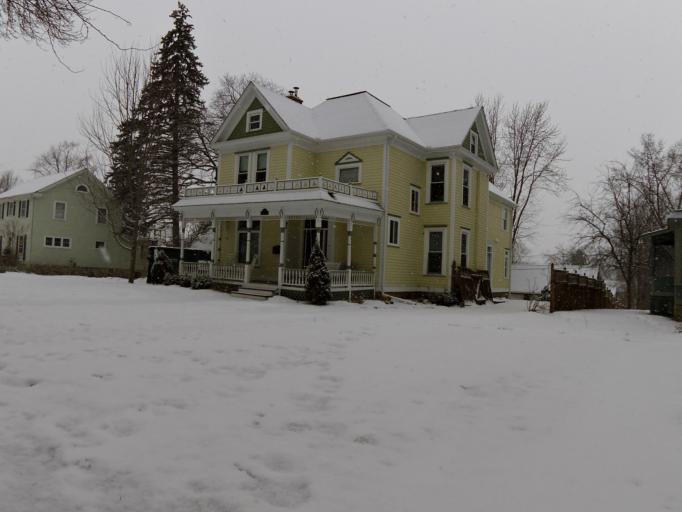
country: US
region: Wisconsin
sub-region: Saint Croix County
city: Hudson
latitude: 44.9832
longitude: -92.7558
